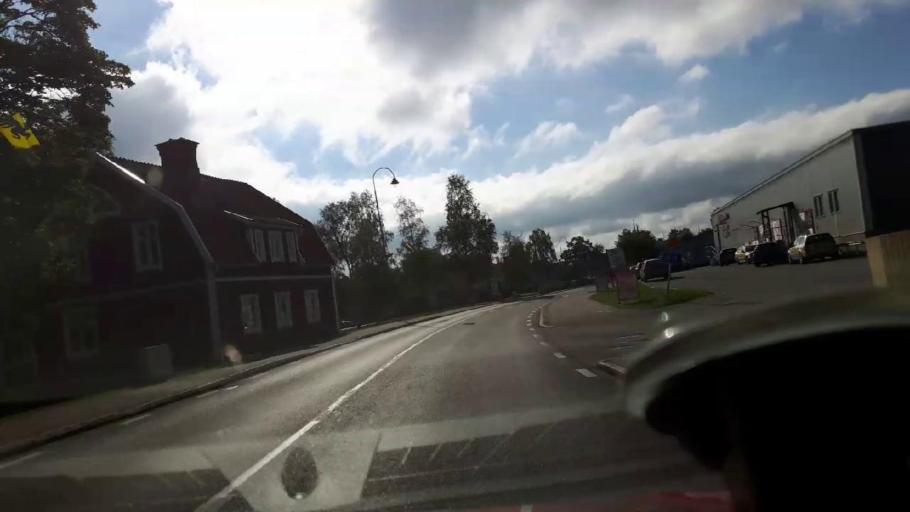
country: SE
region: Gaevleborg
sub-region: Ljusdals Kommun
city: Jaervsoe
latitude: 61.7184
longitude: 16.1701
